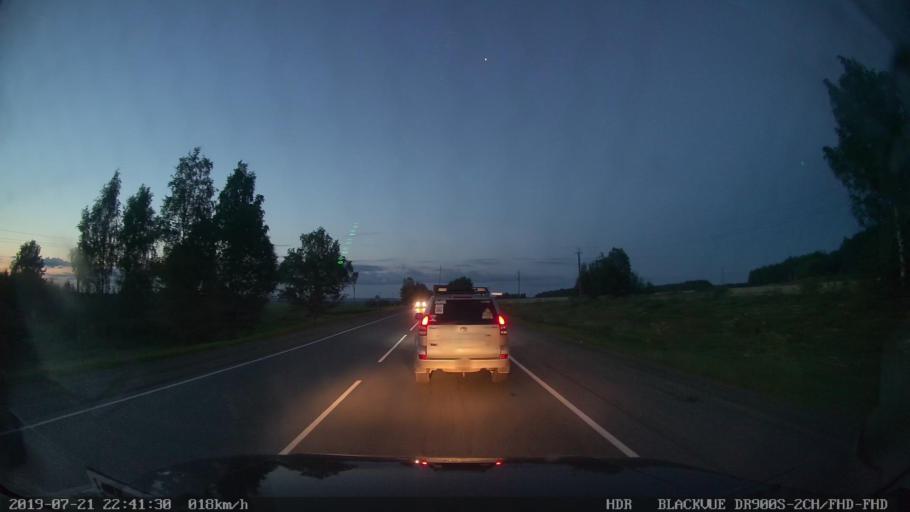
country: RU
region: Perm
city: Ust'-Kachka
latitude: 58.0499
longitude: 55.5918
